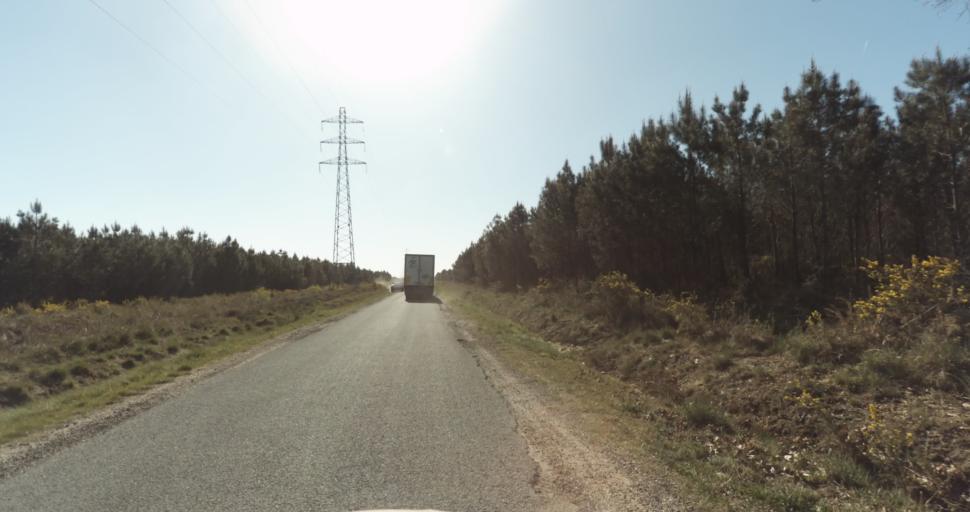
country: FR
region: Aquitaine
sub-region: Departement de la Gironde
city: Marcheprime
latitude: 44.7498
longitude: -0.8457
